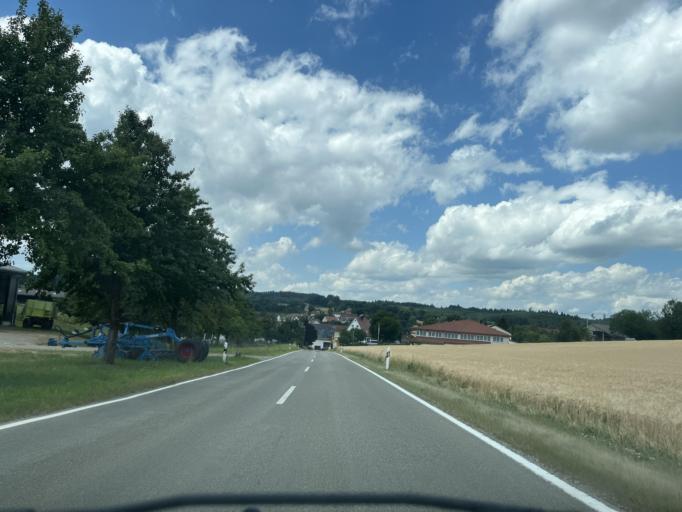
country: DE
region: Baden-Wuerttemberg
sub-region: Tuebingen Region
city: Leibertingen
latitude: 48.0429
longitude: 9.0198
